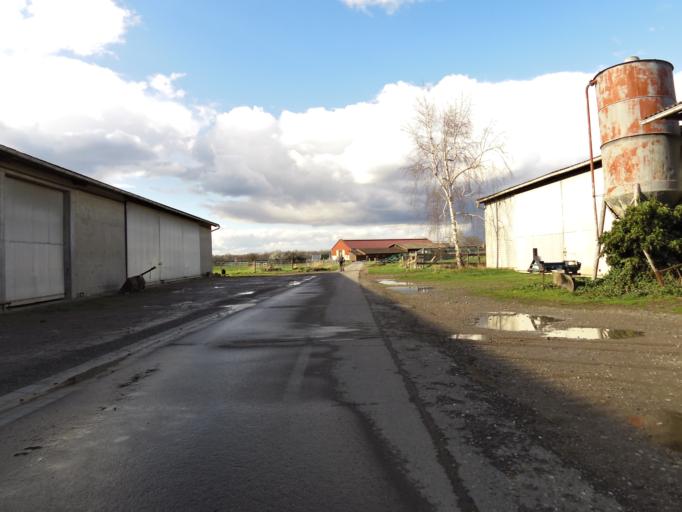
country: DE
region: Rheinland-Pfalz
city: Worms
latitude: 49.6856
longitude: 8.3858
